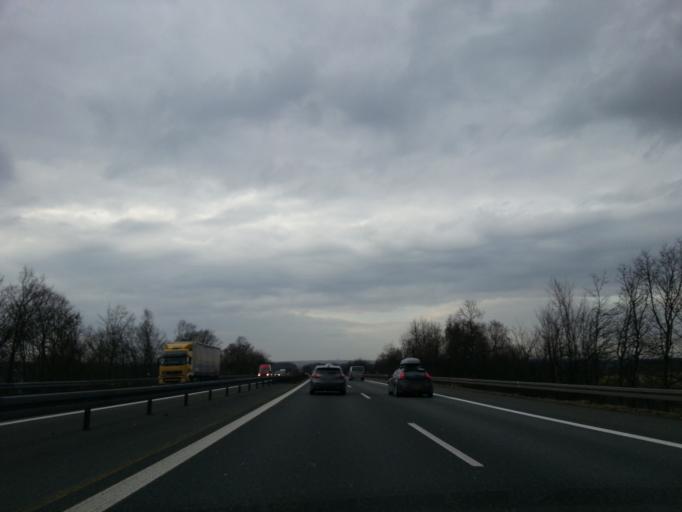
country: DE
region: Bavaria
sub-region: Regierungsbezirk Unterfranken
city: Kleinlangheim
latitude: 49.7792
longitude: 10.2997
